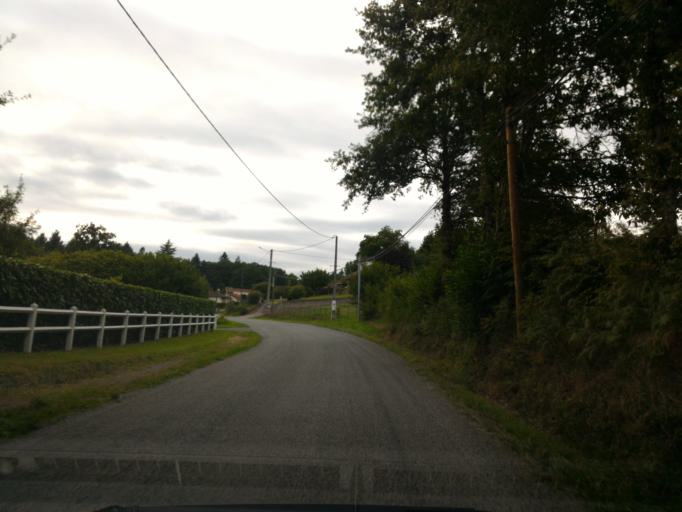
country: FR
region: Limousin
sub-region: Departement de la Haute-Vienne
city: Saint-Junien
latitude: 45.8986
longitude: 0.8743
